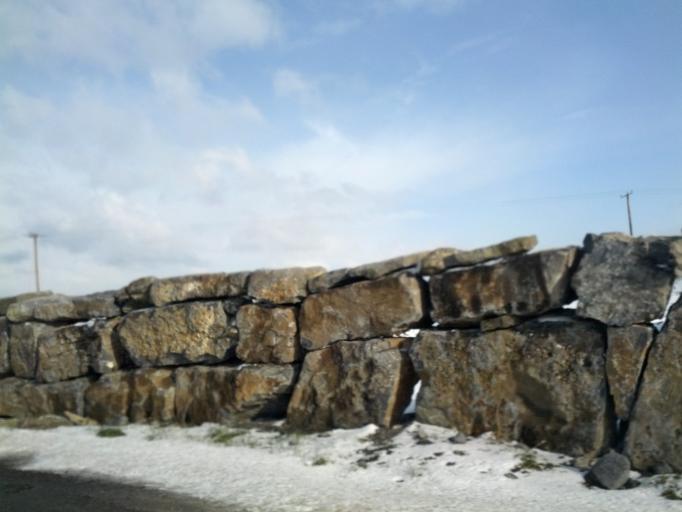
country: IE
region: Connaught
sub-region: County Galway
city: Athenry
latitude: 53.2046
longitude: -8.7603
